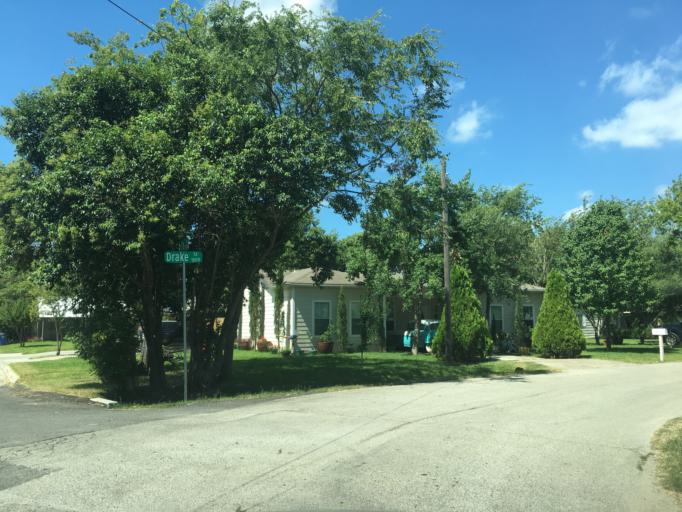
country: US
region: Texas
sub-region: Dallas County
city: Garland
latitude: 32.8351
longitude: -96.6869
